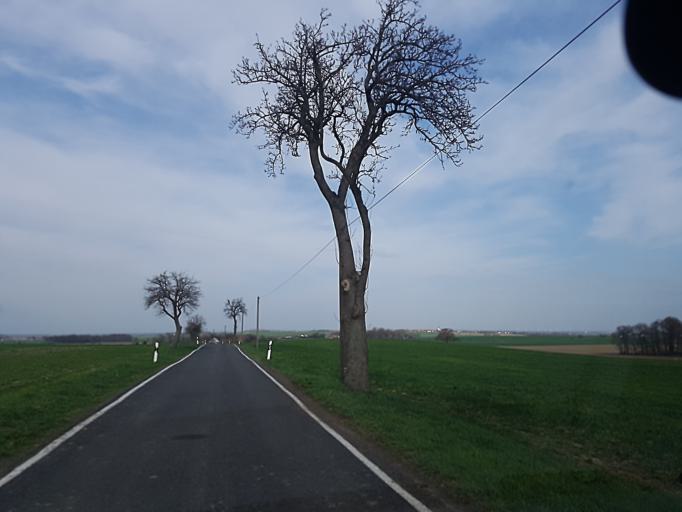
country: DE
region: Saxony
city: Cavertitz
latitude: 51.3471
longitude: 13.1656
